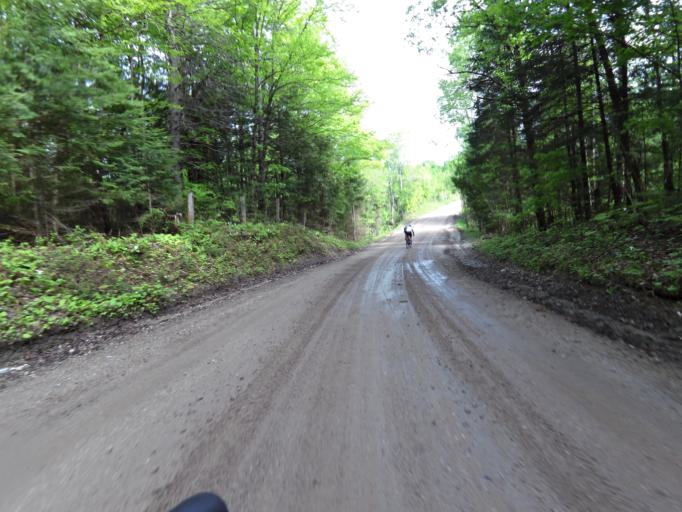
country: CA
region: Quebec
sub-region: Outaouais
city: Wakefield
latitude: 45.7109
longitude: -75.8944
